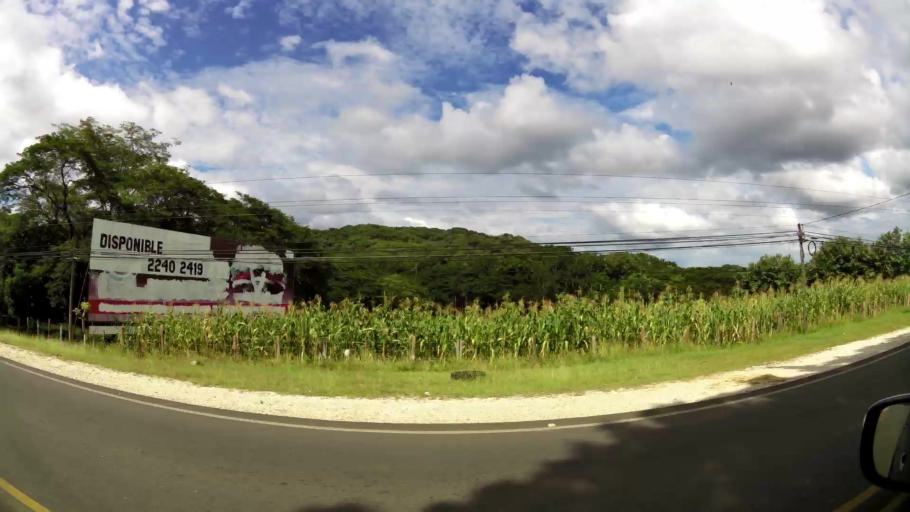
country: CR
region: Guanacaste
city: Hojancha
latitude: 10.1108
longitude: -85.3536
